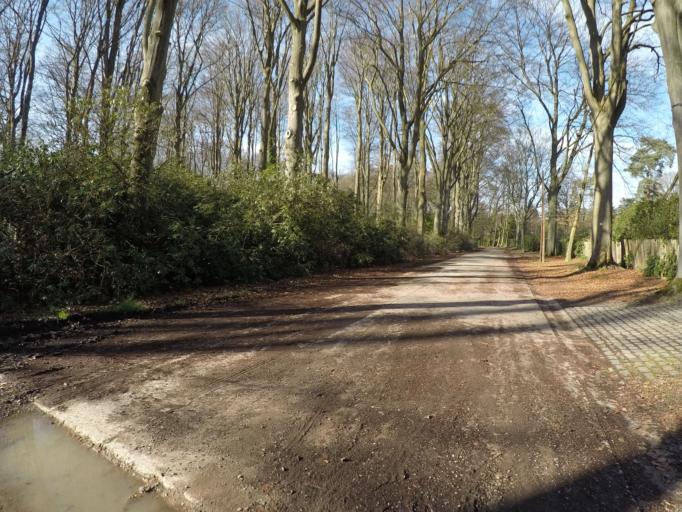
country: BE
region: Flanders
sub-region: Provincie Antwerpen
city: Wijnegem
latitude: 51.2347
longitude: 4.5419
